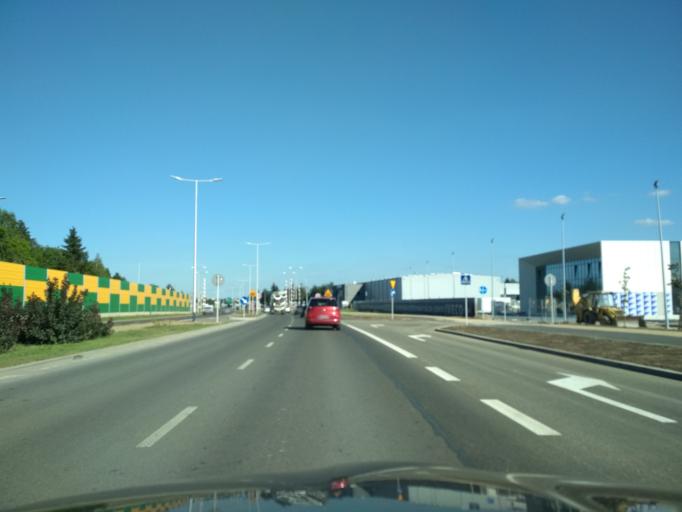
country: PL
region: Subcarpathian Voivodeship
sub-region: Powiat rzeszowski
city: Trzebownisko
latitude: 50.0570
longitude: 22.0271
